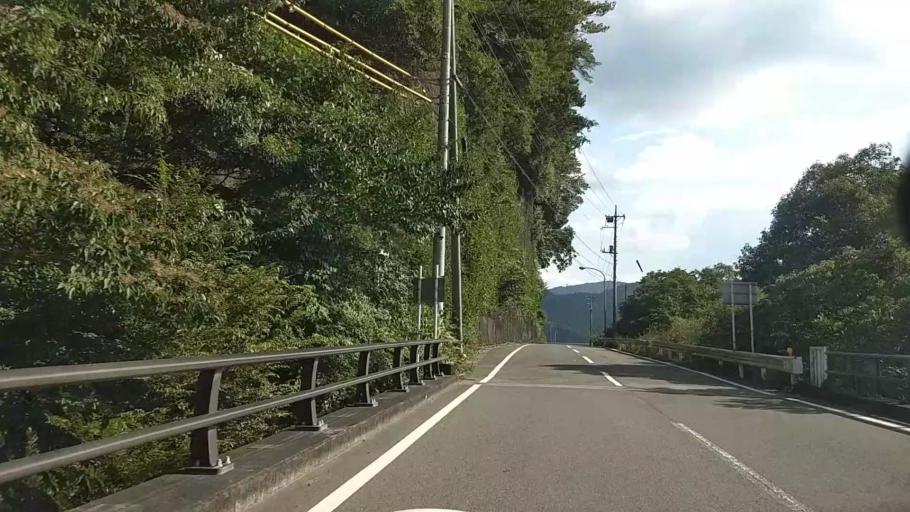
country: JP
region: Shizuoka
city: Fujinomiya
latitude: 35.2881
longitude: 138.4600
